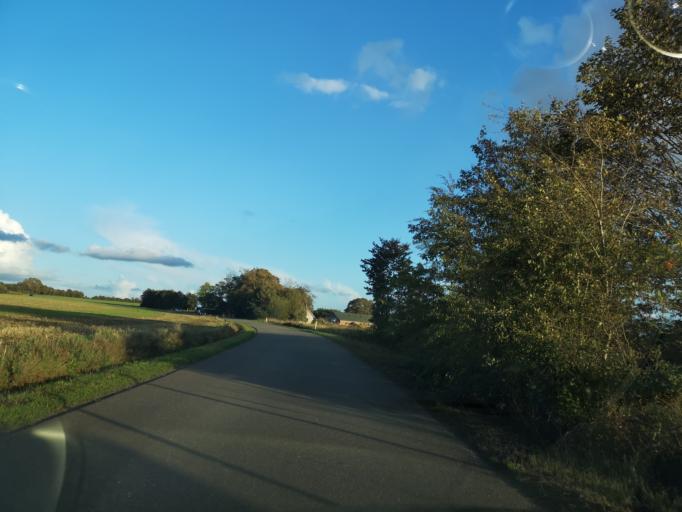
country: DK
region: Central Jutland
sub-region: Ringkobing-Skjern Kommune
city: Skjern
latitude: 55.9863
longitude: 8.5328
